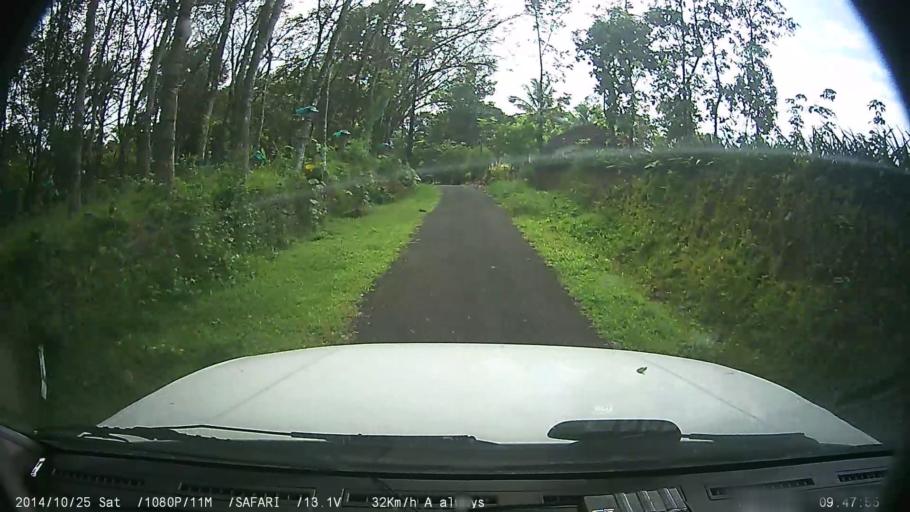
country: IN
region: Kerala
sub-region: Kottayam
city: Palackattumala
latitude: 9.7887
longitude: 76.5692
